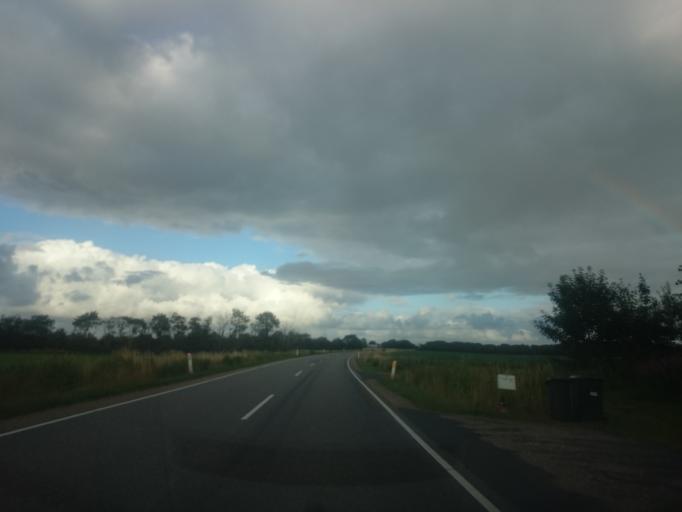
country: DK
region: South Denmark
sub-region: Varde Kommune
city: Olgod
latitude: 55.6655
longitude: 8.7479
